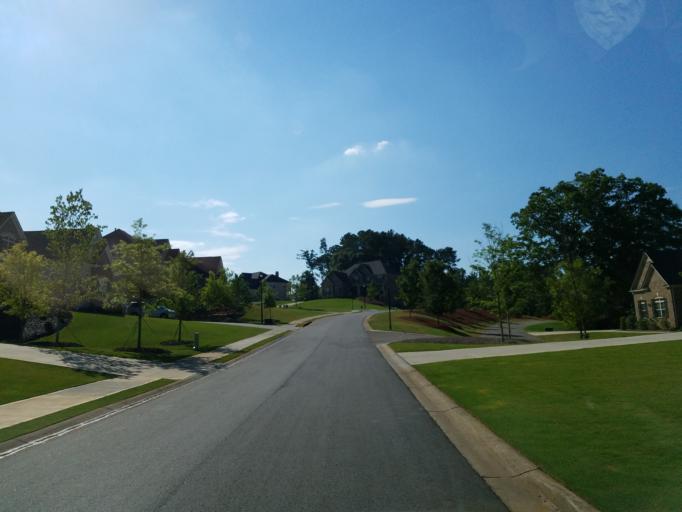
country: US
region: Georgia
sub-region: Fulton County
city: Milton
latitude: 34.1819
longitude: -84.3253
